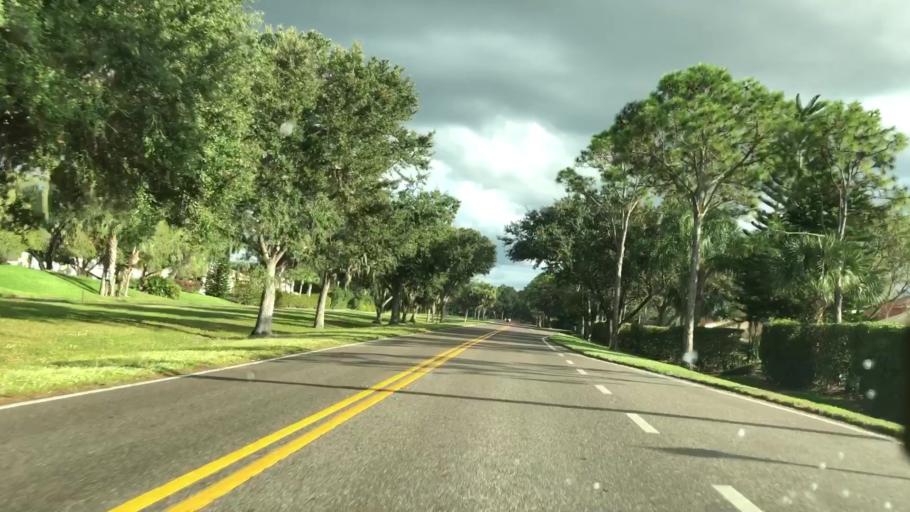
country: US
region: Florida
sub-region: Sarasota County
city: The Meadows
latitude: 27.3718
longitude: -82.4626
